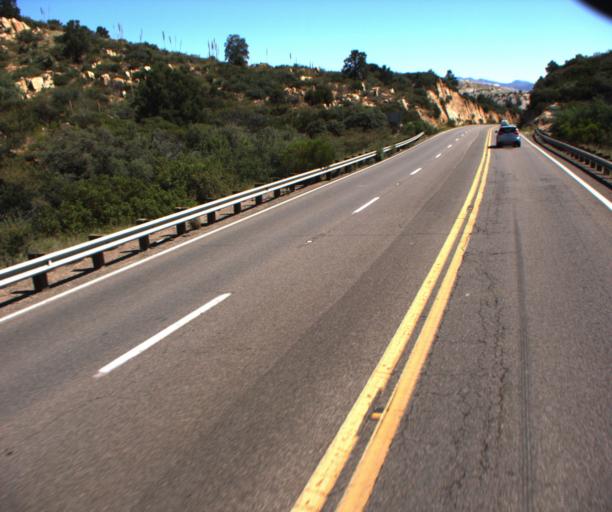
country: US
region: Arizona
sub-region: Gila County
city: Miami
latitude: 33.3711
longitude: -110.9216
